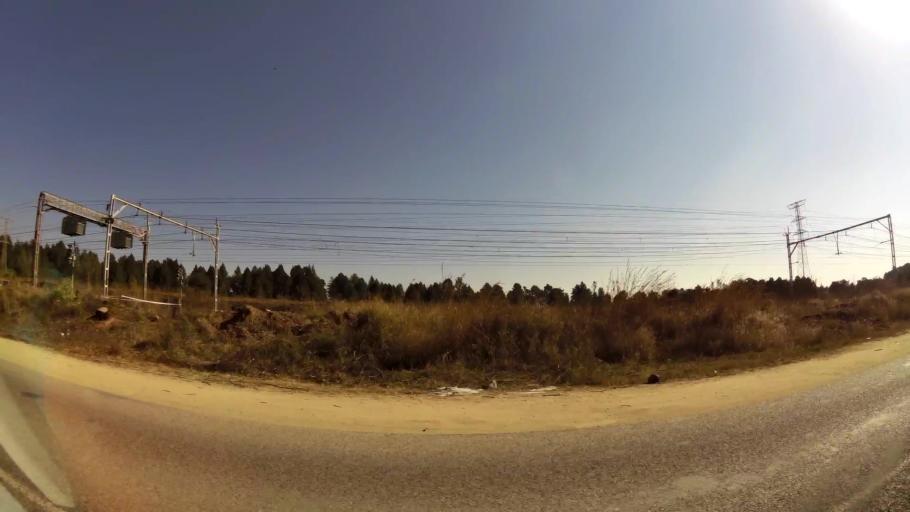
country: ZA
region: Gauteng
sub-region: Ekurhuleni Metropolitan Municipality
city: Tembisa
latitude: -26.0510
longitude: 28.2494
